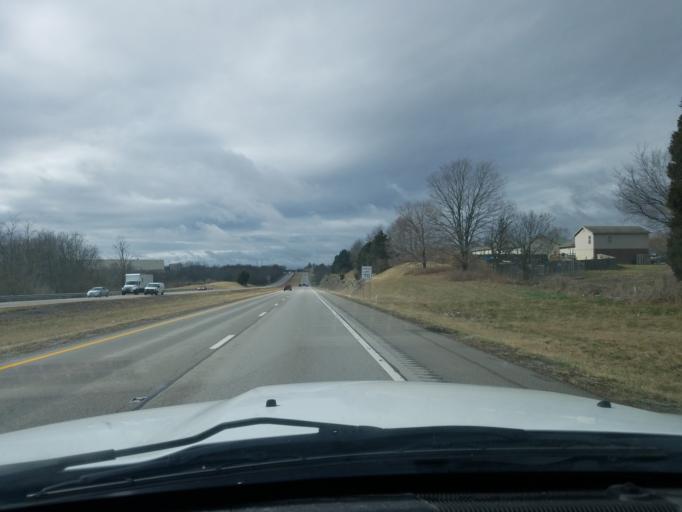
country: US
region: Kentucky
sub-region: Montgomery County
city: Mount Sterling
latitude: 38.0874
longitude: -83.9102
